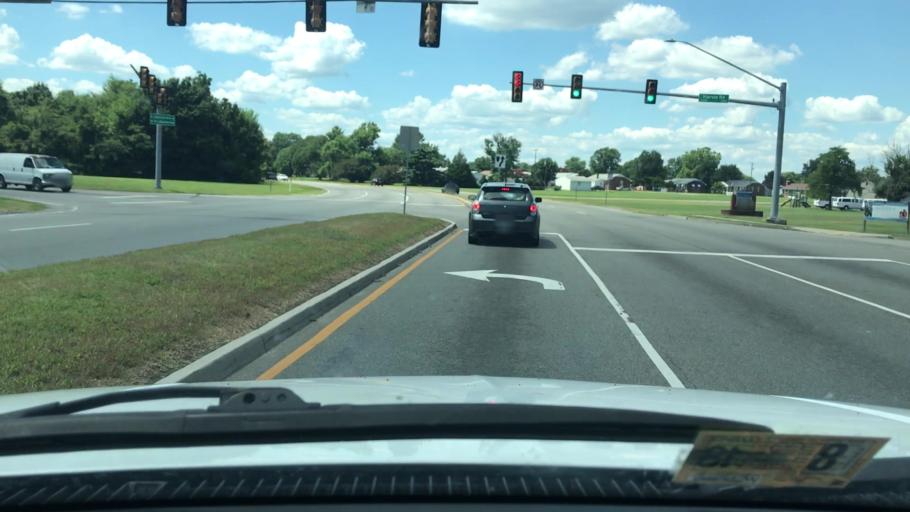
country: US
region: Virginia
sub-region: Henrico County
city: East Highland Park
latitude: 37.5716
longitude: -77.3821
